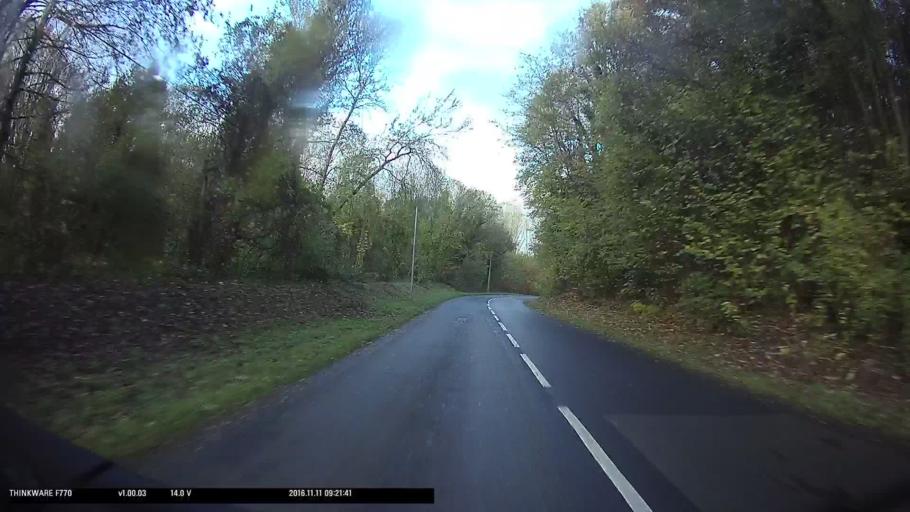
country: FR
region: Ile-de-France
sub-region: Departement du Val-d'Oise
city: Ableiges
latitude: 49.0862
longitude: 1.9956
